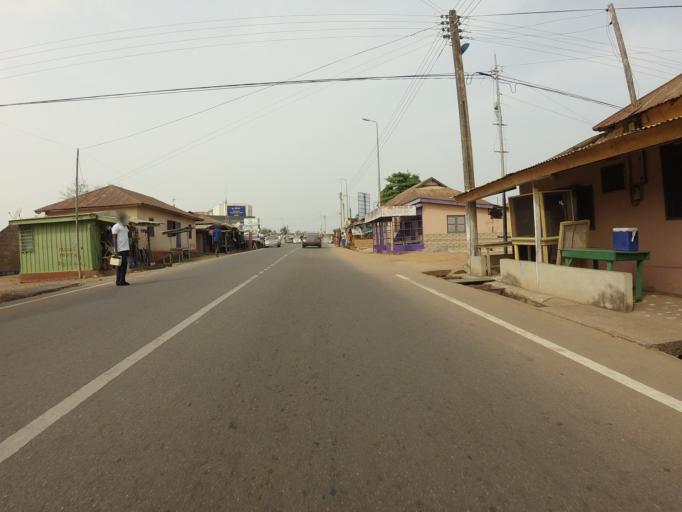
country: GH
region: Volta
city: Ho
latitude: 6.6073
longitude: 0.4737
